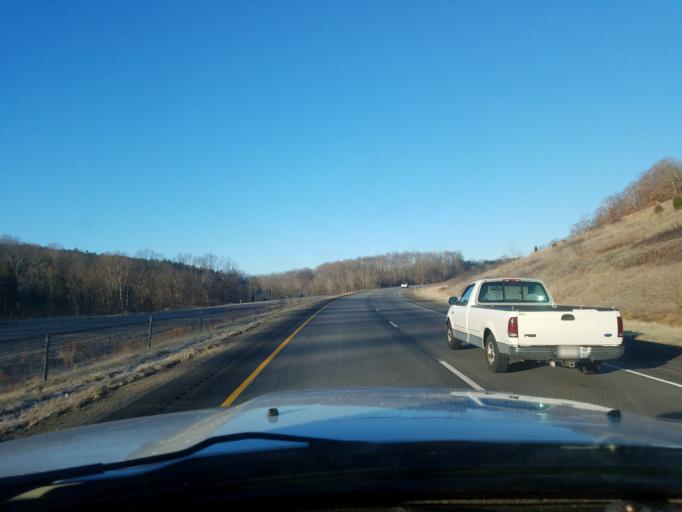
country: US
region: Indiana
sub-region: Crawford County
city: English
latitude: 38.2271
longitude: -86.6395
